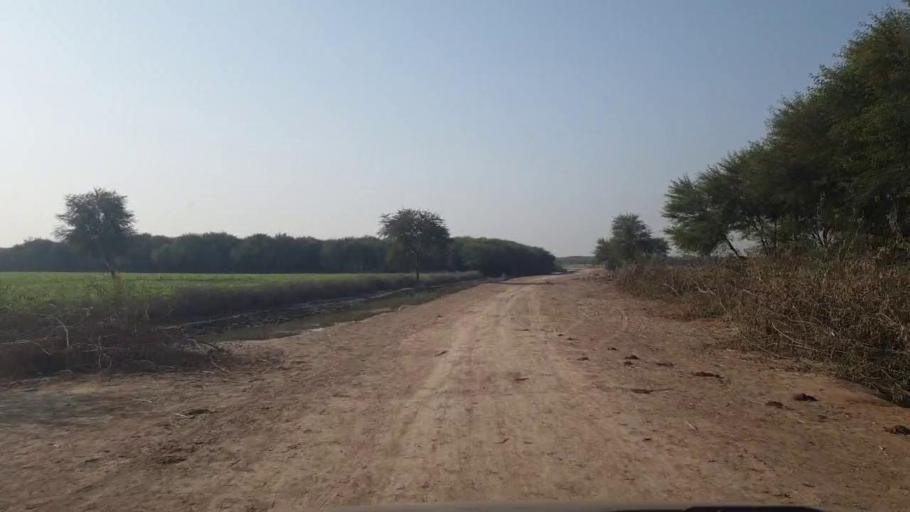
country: PK
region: Sindh
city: Tando Adam
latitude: 25.7240
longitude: 68.6060
